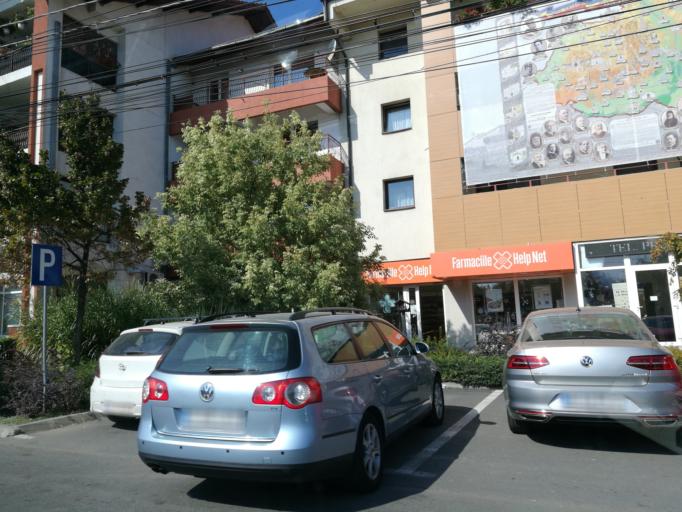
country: RO
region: Ilfov
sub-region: Comuna Otopeni
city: Otopeni
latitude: 44.5512
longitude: 26.0732
